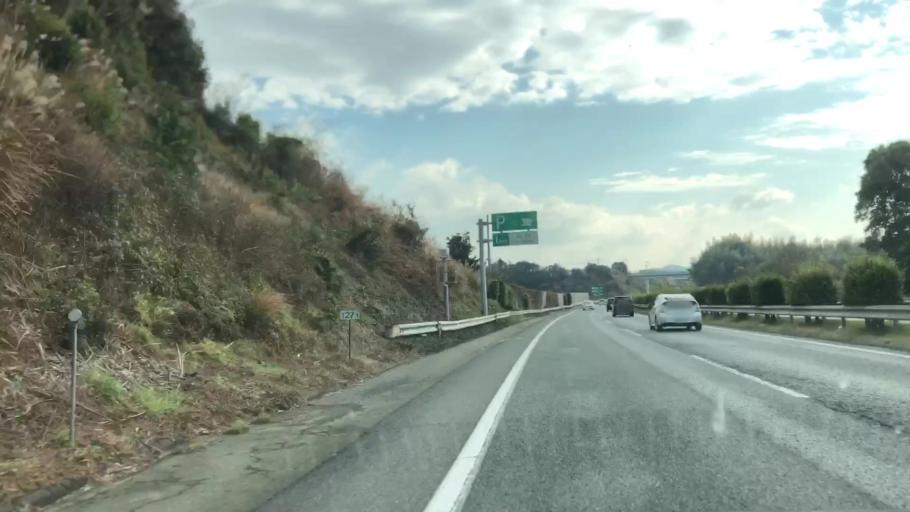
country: JP
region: Fukuoka
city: Setakamachi-takayanagi
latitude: 33.1369
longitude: 130.5153
